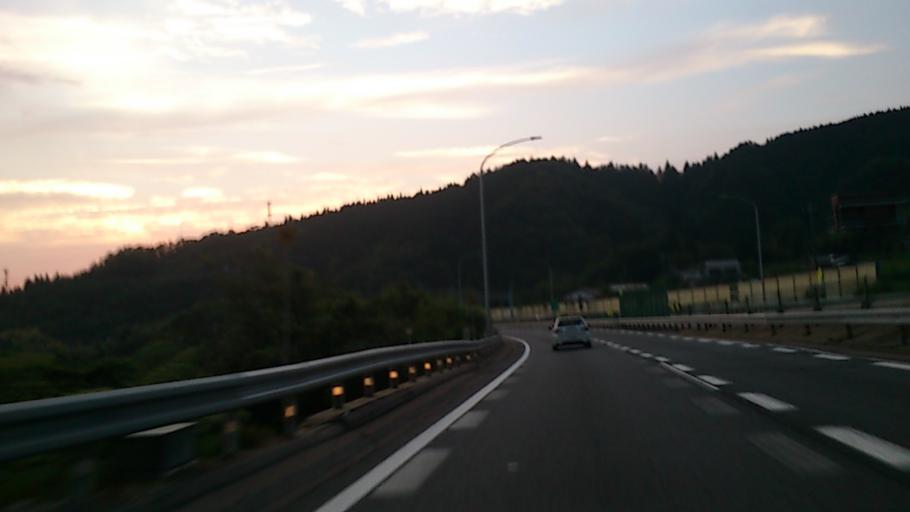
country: JP
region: Gifu
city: Nakatsugawa
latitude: 35.5111
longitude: 137.5855
